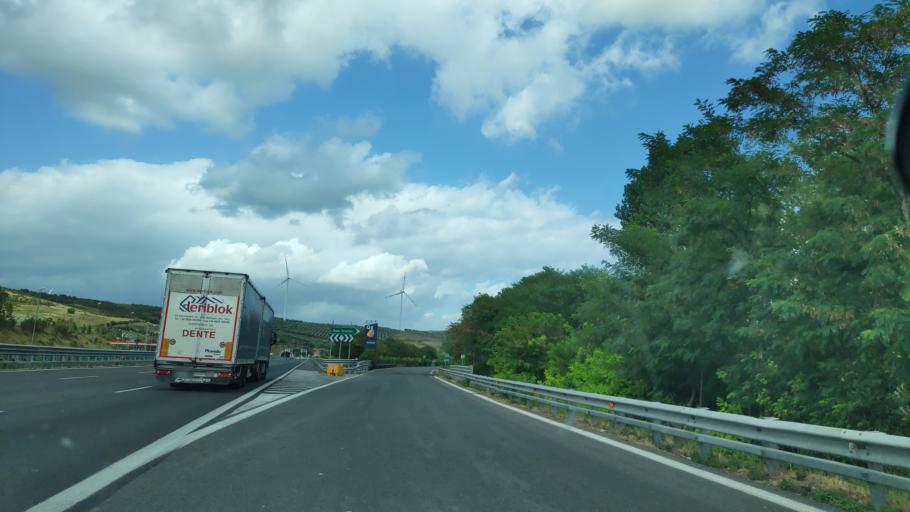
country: IT
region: Campania
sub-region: Provincia di Salerno
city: Serre
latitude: 40.6167
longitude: 15.1625
